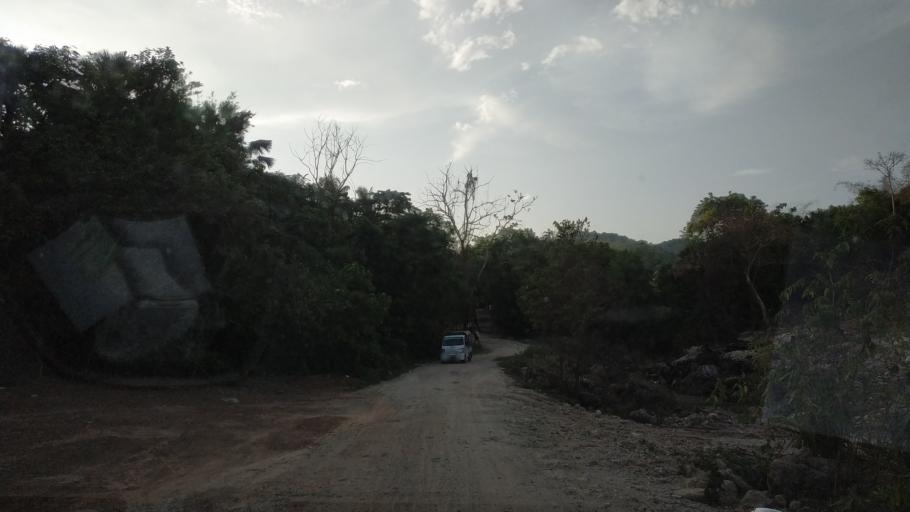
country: MM
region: Mon
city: Kyaikto
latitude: 17.4352
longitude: 97.0407
